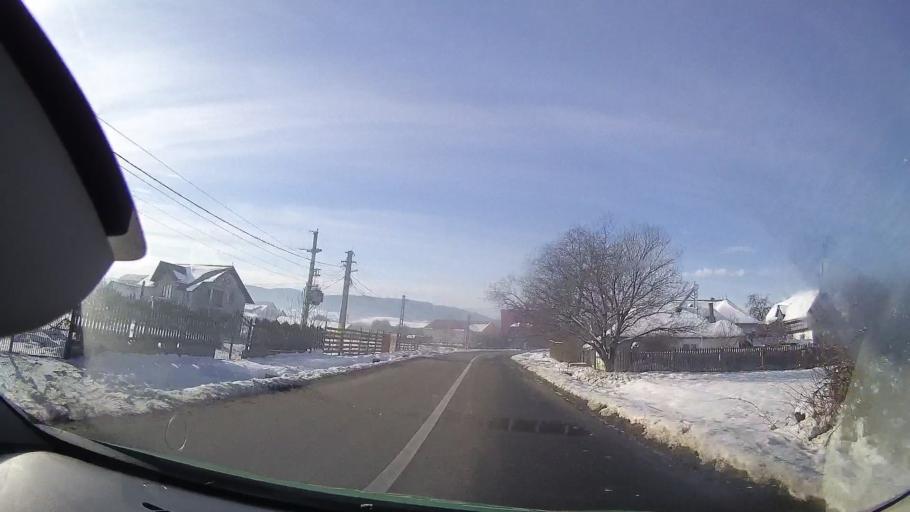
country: RO
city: Vanatori-Neamt
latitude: 47.1732
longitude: 26.3126
